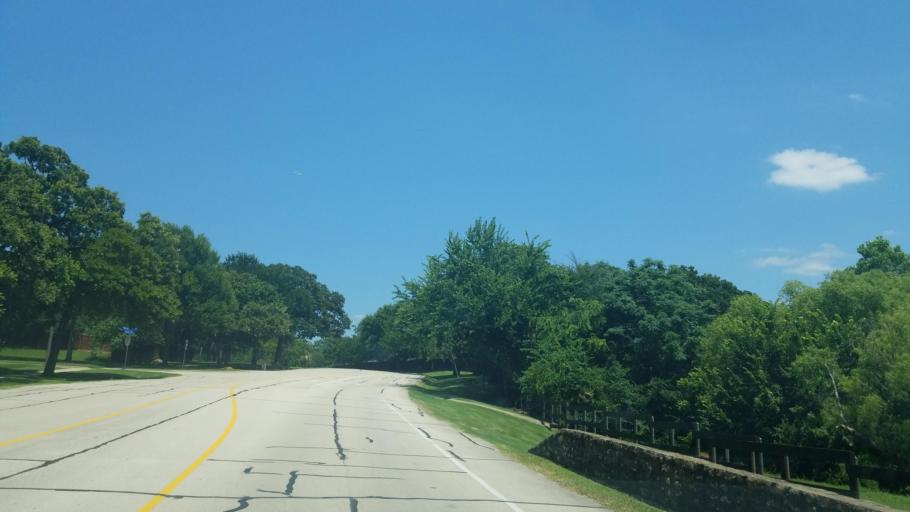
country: US
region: Texas
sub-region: Denton County
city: Highland Village
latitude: 33.0842
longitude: -97.0602
